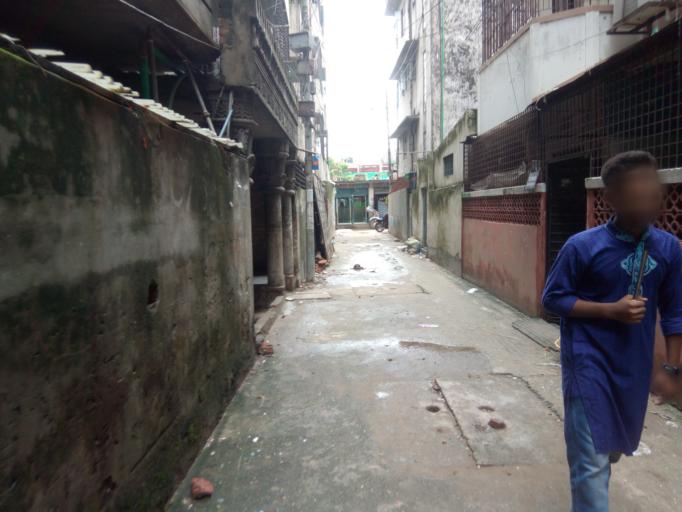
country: BD
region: Dhaka
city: Azimpur
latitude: 23.7451
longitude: 90.3674
